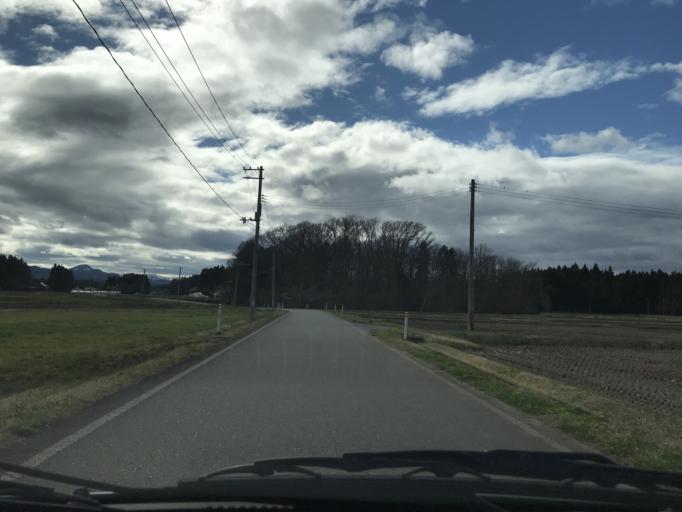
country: JP
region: Iwate
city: Mizusawa
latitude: 39.1105
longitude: 141.0860
